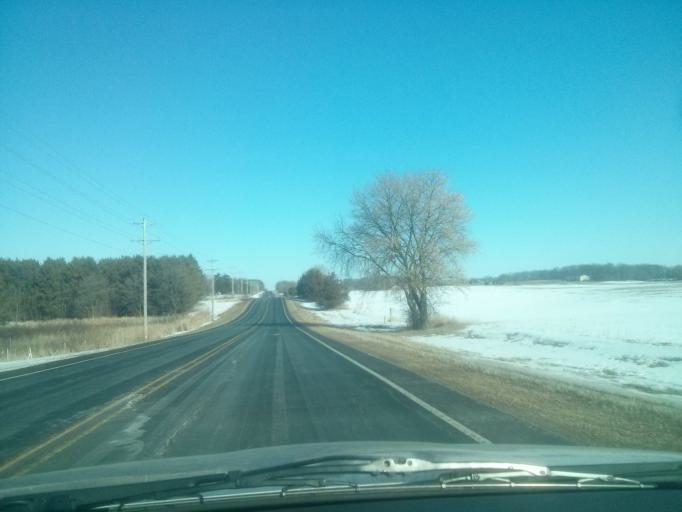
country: US
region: Minnesota
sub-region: Washington County
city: Bayport
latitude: 45.0729
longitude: -92.7361
